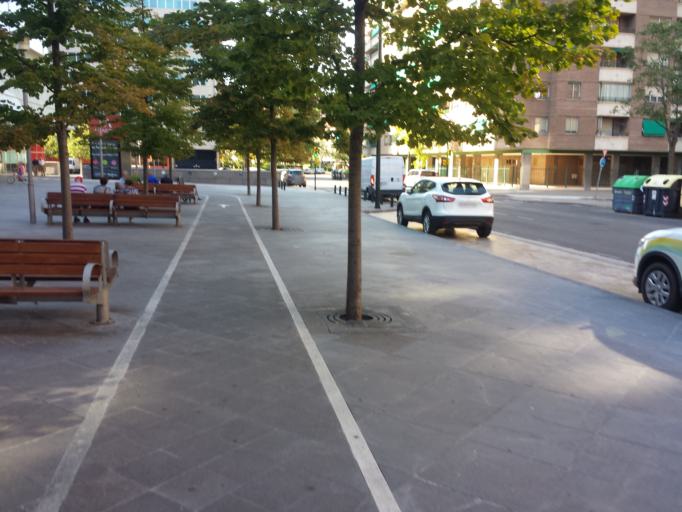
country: ES
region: Aragon
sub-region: Provincia de Zaragoza
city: Delicias
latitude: 41.6406
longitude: -0.9090
